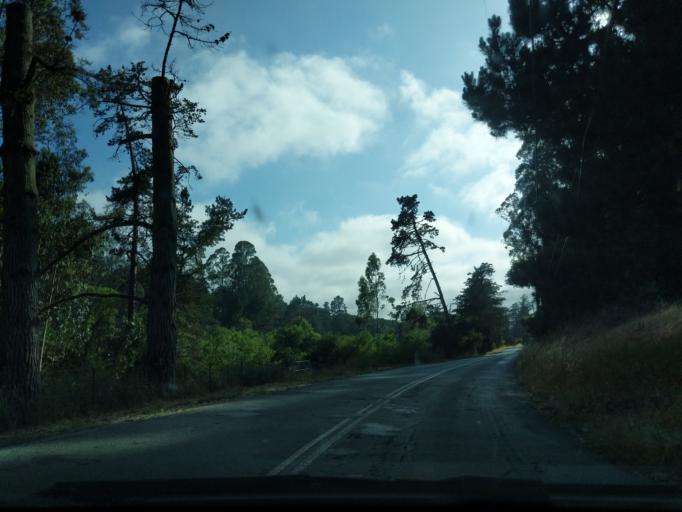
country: US
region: California
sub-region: Monterey County
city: Prunedale
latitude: 36.7984
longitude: -121.6449
